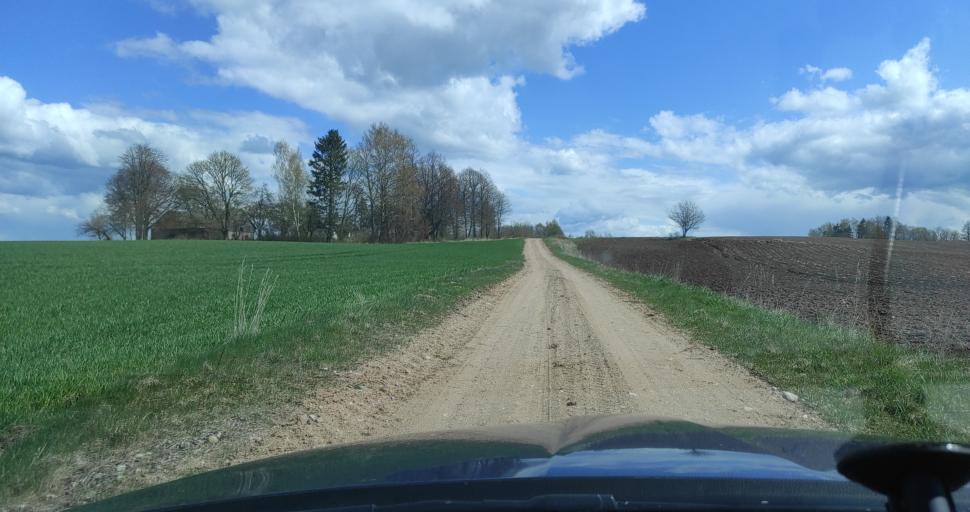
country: LV
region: Kuldigas Rajons
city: Kuldiga
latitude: 56.8688
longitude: 21.7971
